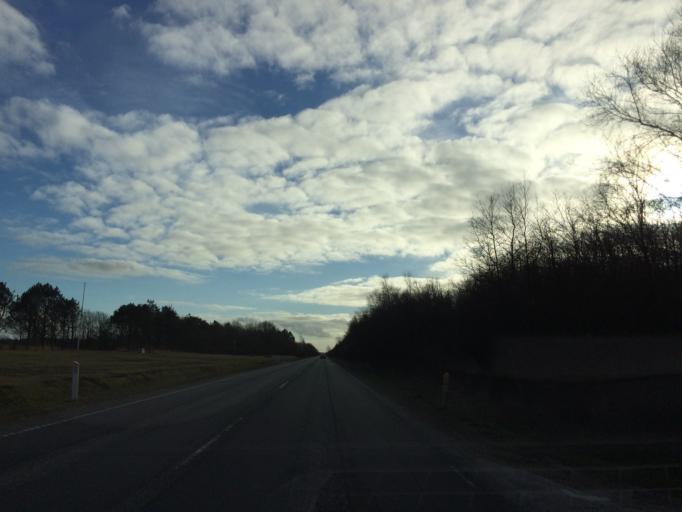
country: DK
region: Central Jutland
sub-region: Lemvig Kommune
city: Lemvig
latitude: 56.5058
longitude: 8.3034
